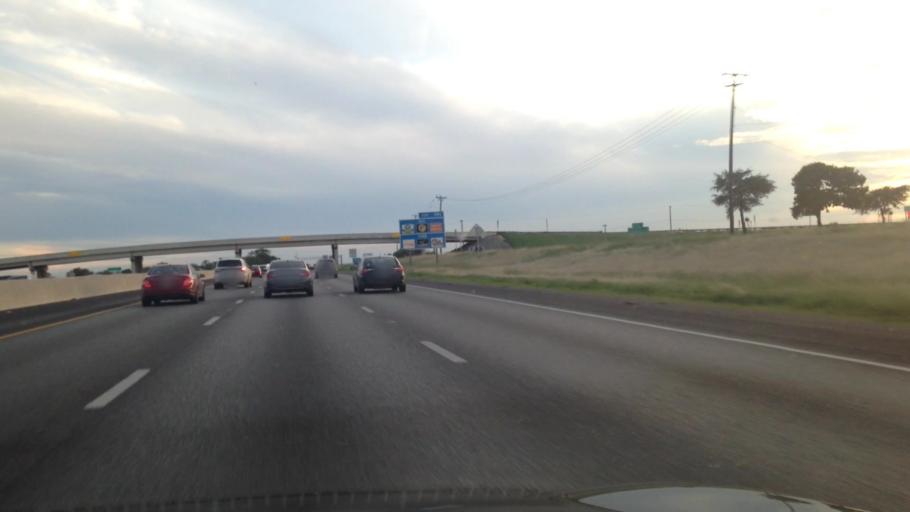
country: US
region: Texas
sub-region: Guadalupe County
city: Lake Dunlap
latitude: 29.7484
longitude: -98.0568
